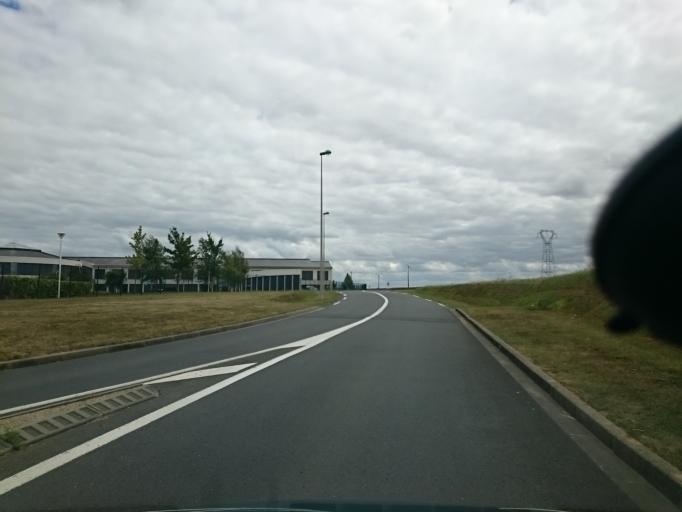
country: FR
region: Lower Normandy
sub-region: Departement du Calvados
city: Ifs
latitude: 49.1353
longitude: -0.3545
